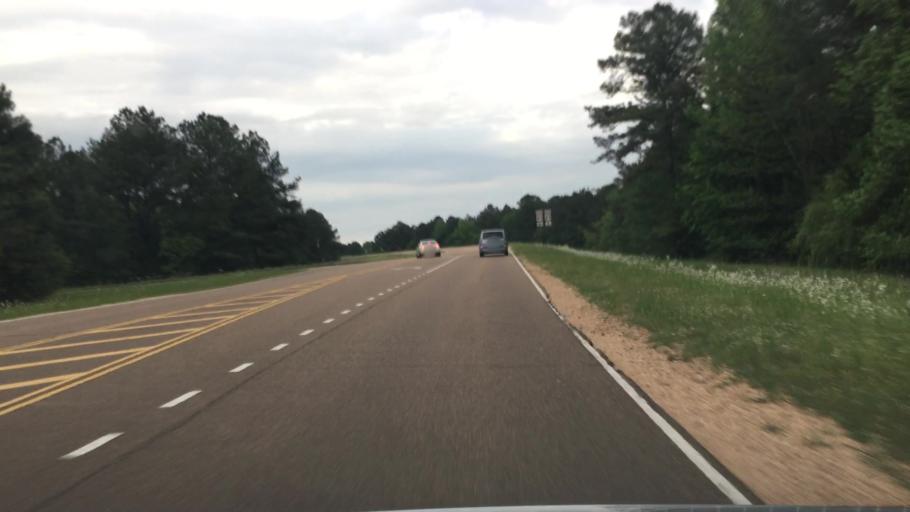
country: US
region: Mississippi
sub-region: Hinds County
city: Clinton
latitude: 32.3802
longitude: -90.2646
